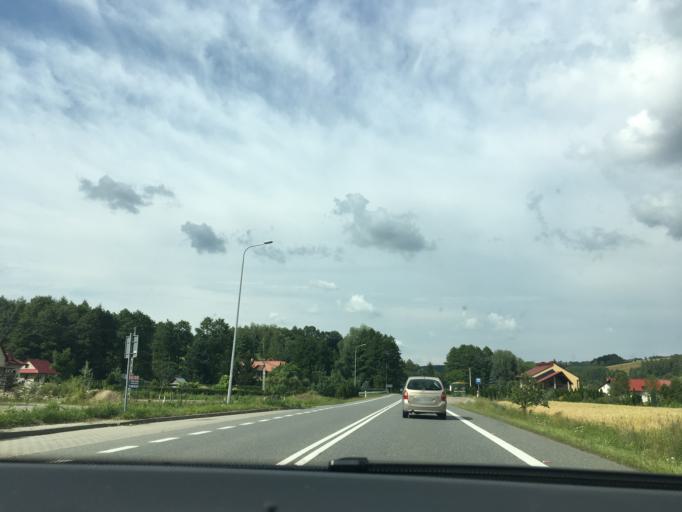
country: PL
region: Subcarpathian Voivodeship
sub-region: Powiat strzyzowski
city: Niebylec
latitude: 49.8675
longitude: 21.9026
